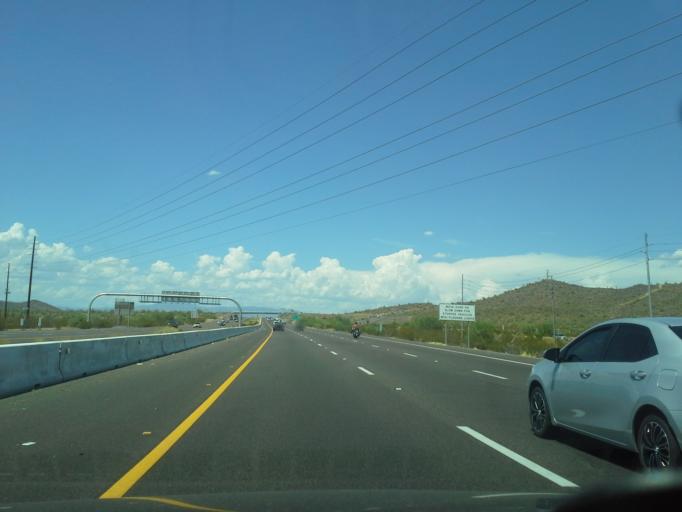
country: US
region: Arizona
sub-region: Maricopa County
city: Anthem
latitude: 33.8116
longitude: -112.1384
